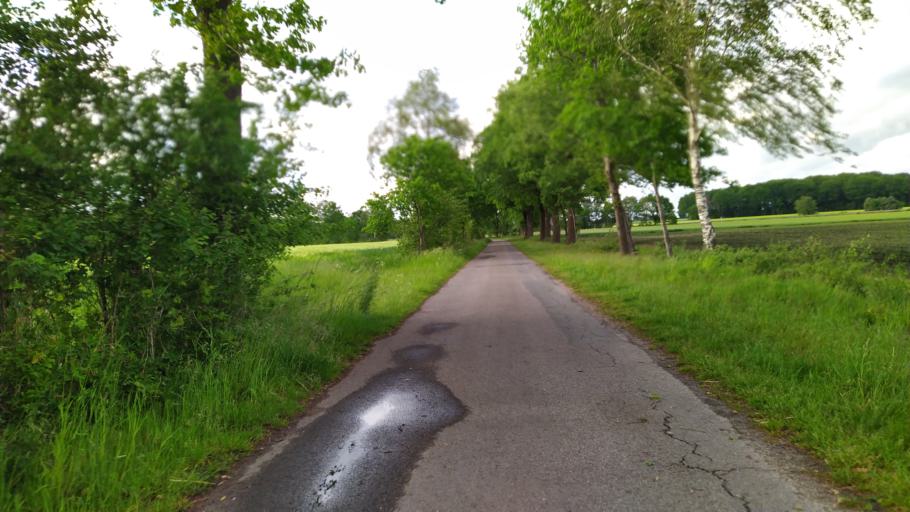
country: DE
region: Lower Saxony
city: Kutenholz
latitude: 53.4666
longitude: 9.3204
